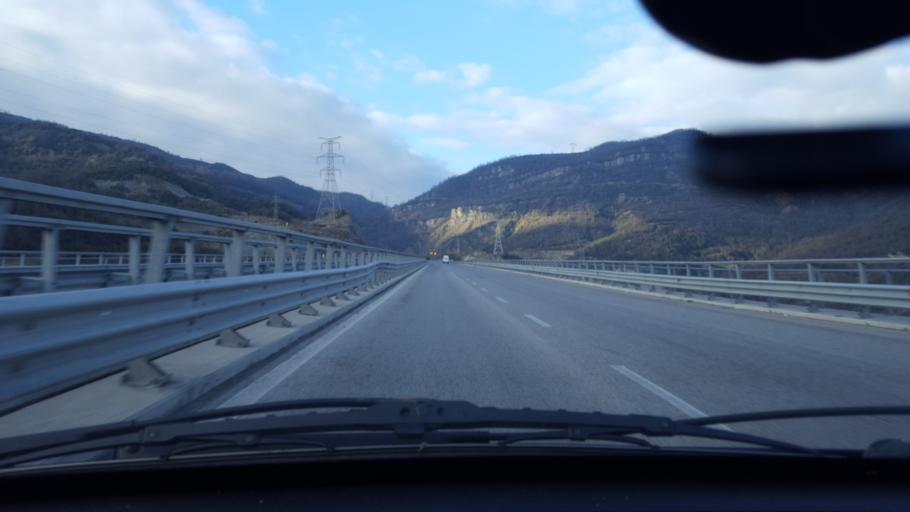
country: AL
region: Tirane
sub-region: Rrethi i Tiranes
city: Krrabe
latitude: 41.1879
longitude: 19.9940
